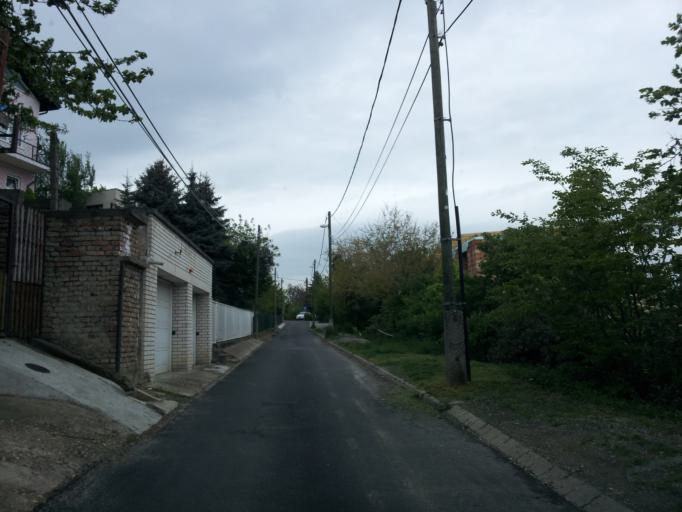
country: HU
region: Budapest
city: Budapest XXII. keruelet
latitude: 47.4373
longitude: 19.0202
